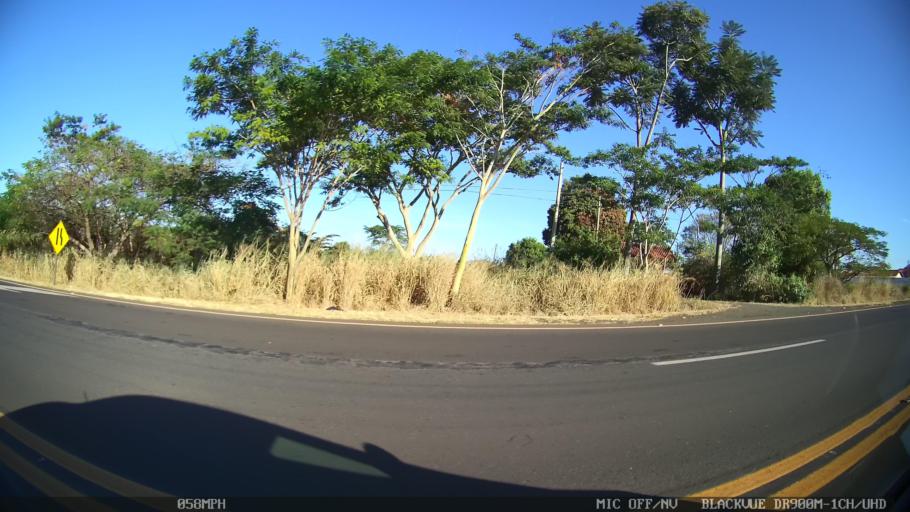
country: BR
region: Sao Paulo
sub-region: Olimpia
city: Olimpia
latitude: -20.7036
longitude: -48.9473
